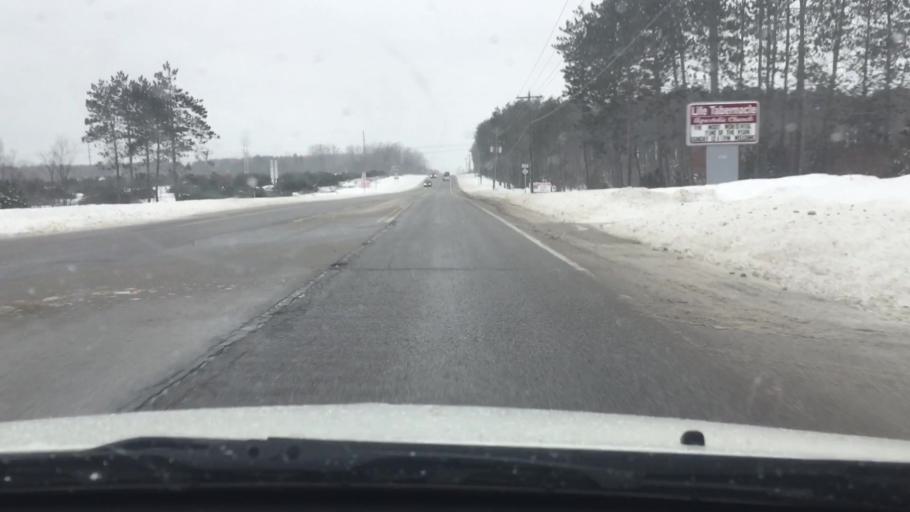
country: US
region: Michigan
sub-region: Otsego County
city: Gaylord
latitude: 45.0276
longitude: -84.7270
